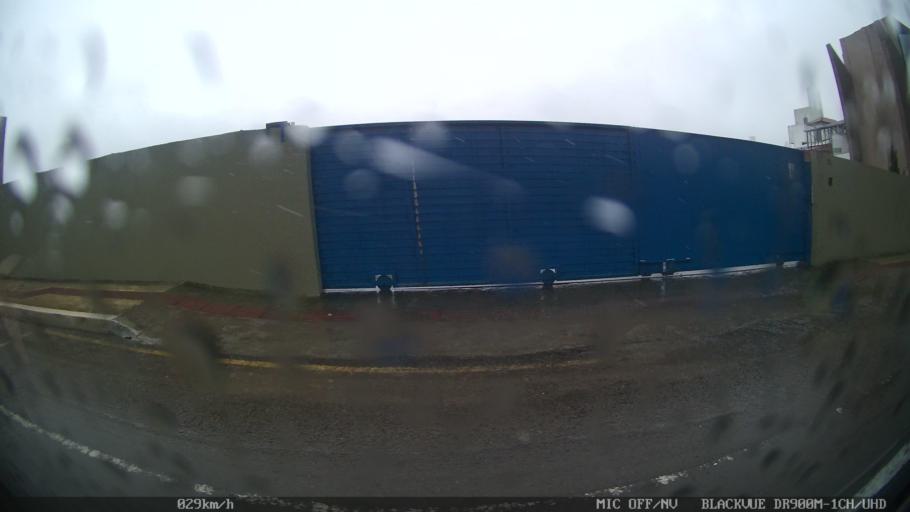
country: BR
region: Santa Catarina
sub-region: Balneario Camboriu
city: Balneario Camboriu
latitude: -27.0081
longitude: -48.6241
